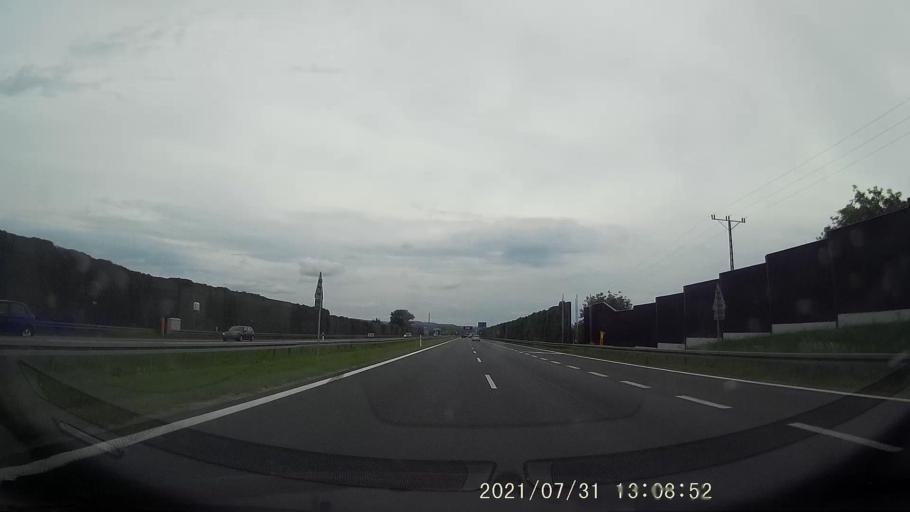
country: PL
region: Lesser Poland Voivodeship
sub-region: Powiat chrzanowski
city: Chrzanow
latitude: 50.1507
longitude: 19.4069
